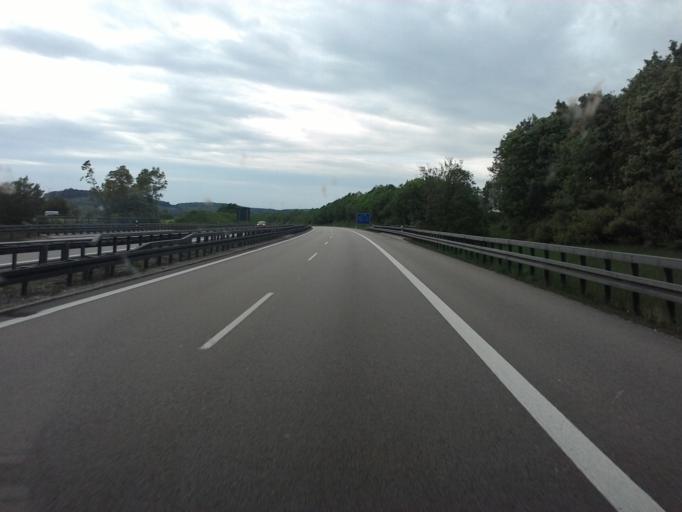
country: DE
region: Bavaria
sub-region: Upper Palatinate
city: Velburg
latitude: 49.2397
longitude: 11.6350
